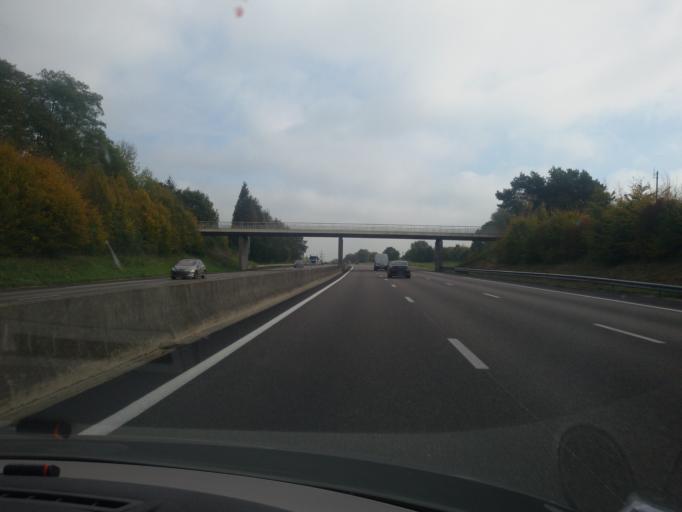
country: FR
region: Haute-Normandie
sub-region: Departement de l'Eure
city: Saint-Ouen-de-Thouberville
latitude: 49.3521
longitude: 0.8893
